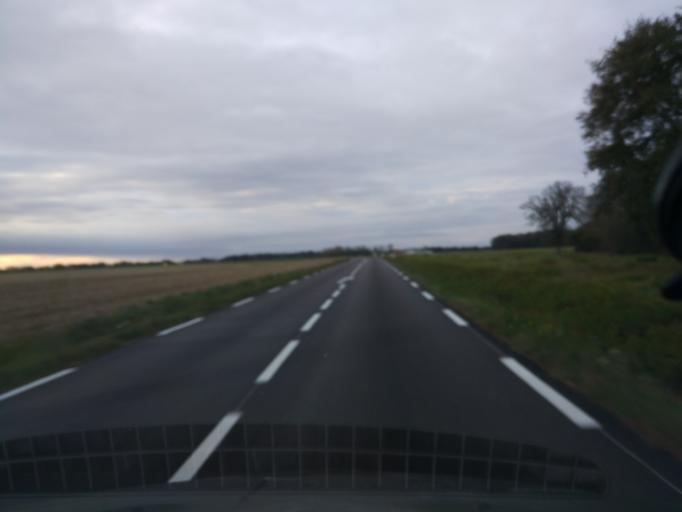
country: FR
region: Ile-de-France
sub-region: Departement de l'Essonne
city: Les Molieres
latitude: 48.6637
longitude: 2.0649
